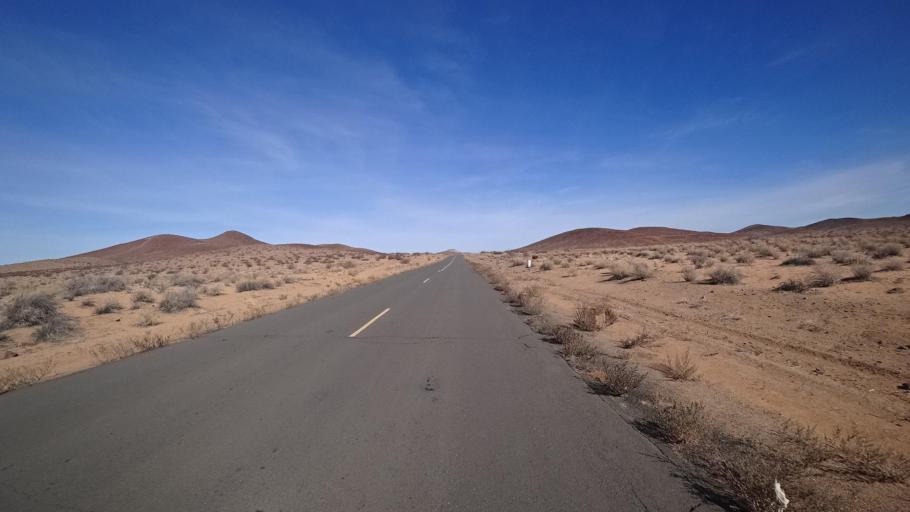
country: US
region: California
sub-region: Kern County
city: North Edwards
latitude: 35.0324
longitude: -117.8288
